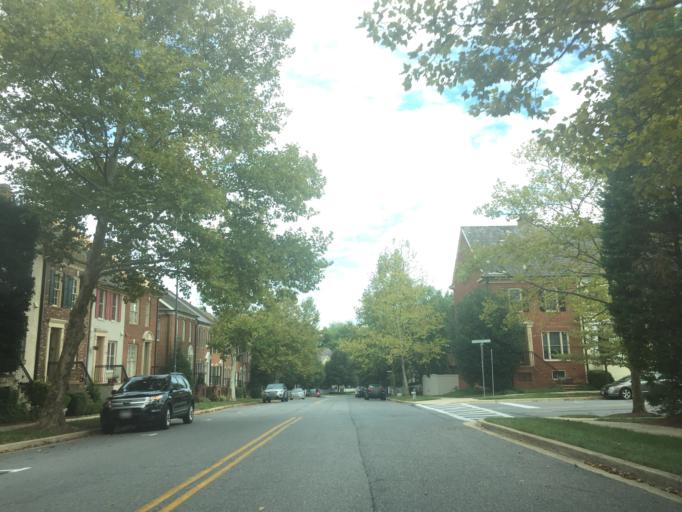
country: US
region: Maryland
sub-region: Montgomery County
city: North Potomac
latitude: 39.1239
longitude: -77.2434
